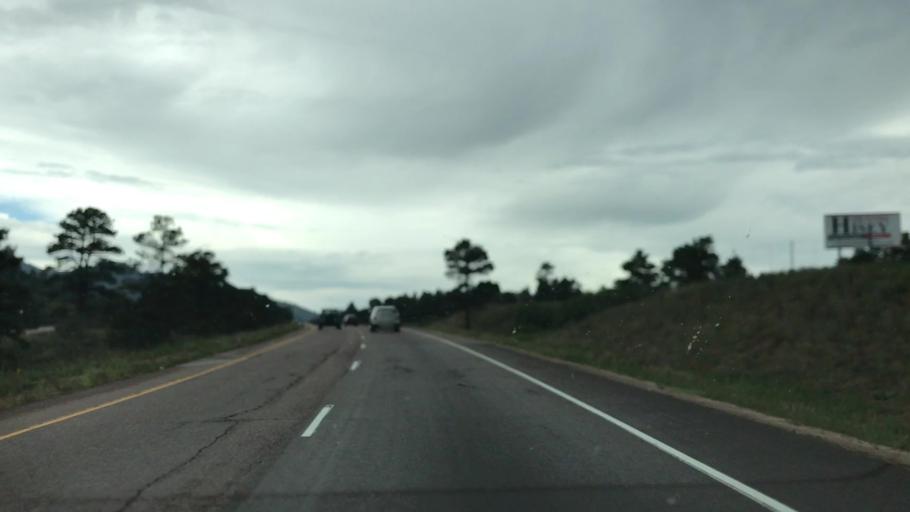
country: US
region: Colorado
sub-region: El Paso County
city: Cascade-Chipita Park
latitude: 38.9324
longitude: -105.0020
